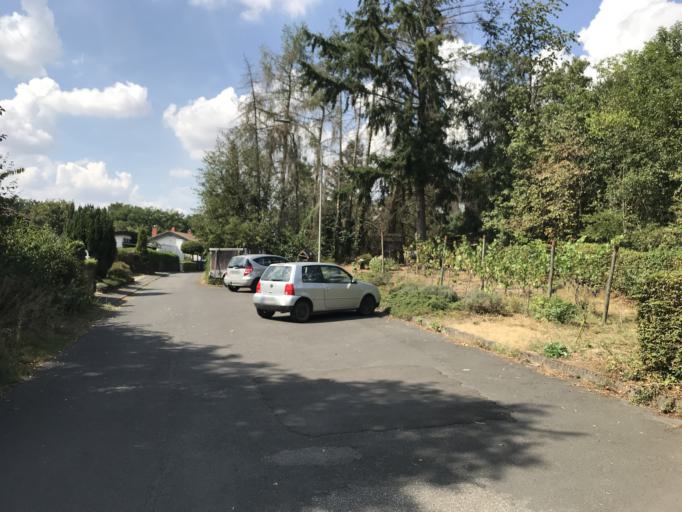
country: DE
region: Hesse
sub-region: Regierungsbezirk Darmstadt
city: Wolfersheim
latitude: 50.4017
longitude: 8.8087
